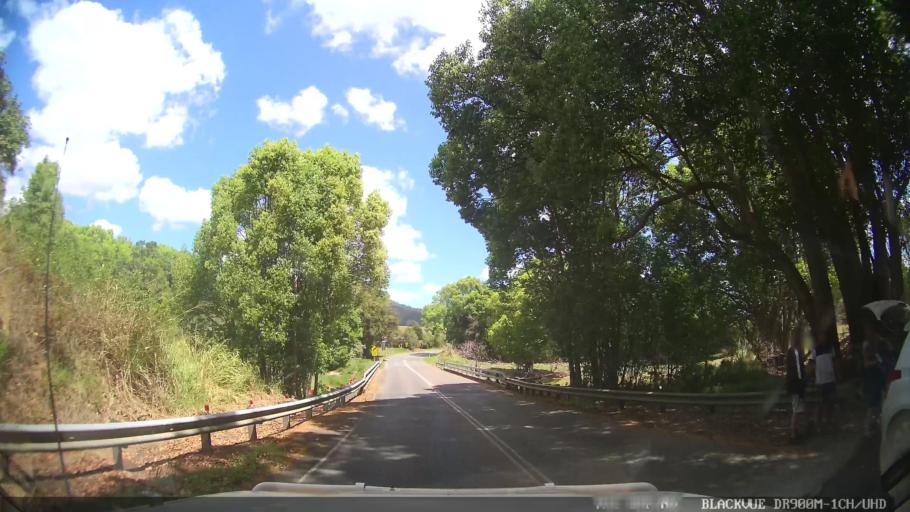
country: AU
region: Queensland
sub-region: Sunshine Coast
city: Nambour
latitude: -26.6481
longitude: 152.8143
